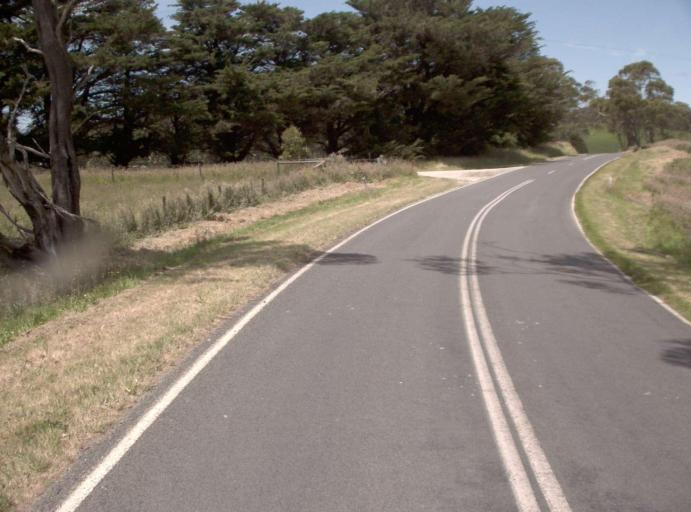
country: AU
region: Victoria
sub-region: Bass Coast
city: North Wonthaggi
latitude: -38.7158
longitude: 146.1025
